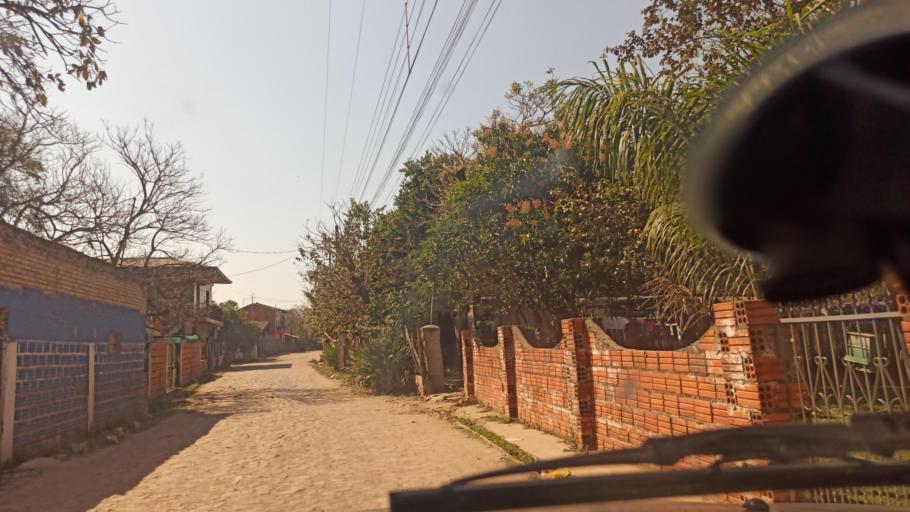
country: AR
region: Formosa
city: Clorinda
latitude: -25.2923
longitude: -57.6969
